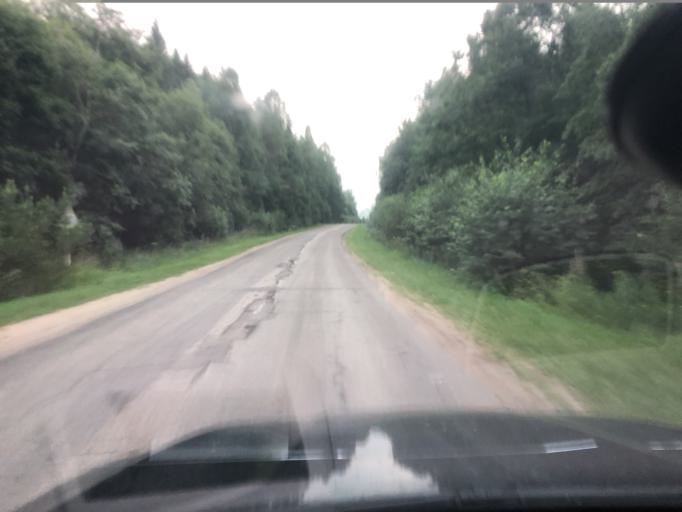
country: RU
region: Jaroslavl
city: Petrovsk
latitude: 56.9984
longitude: 39.0976
